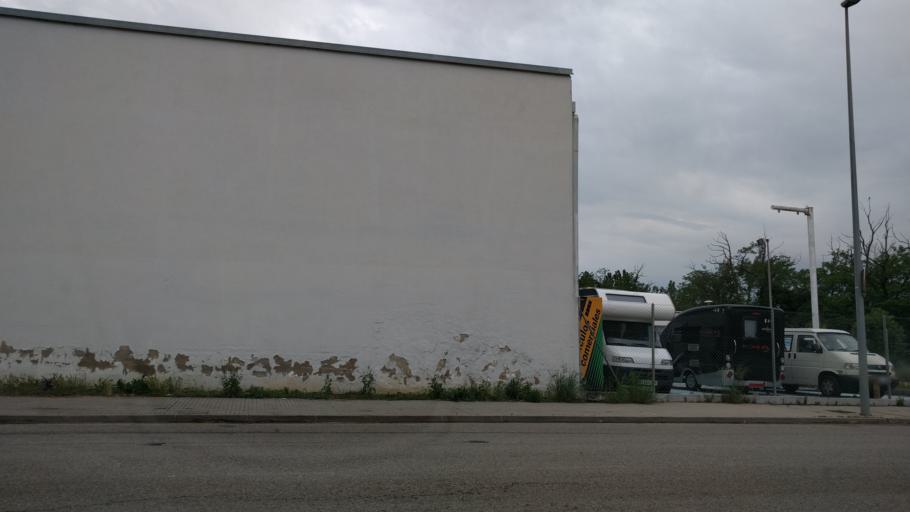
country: ES
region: Catalonia
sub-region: Provincia de Girona
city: Vilablareix
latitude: 41.9702
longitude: 2.7728
